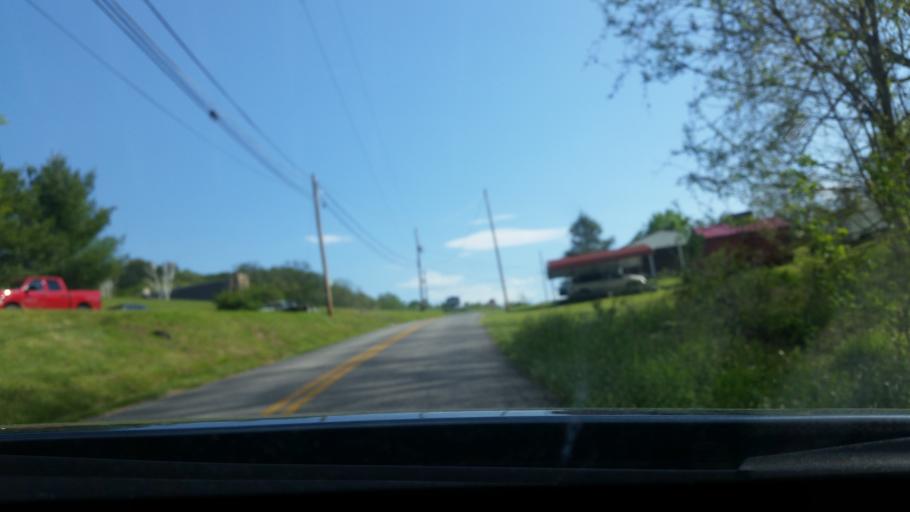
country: US
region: Virginia
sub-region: Giles County
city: Pembroke
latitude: 37.3128
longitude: -80.6317
